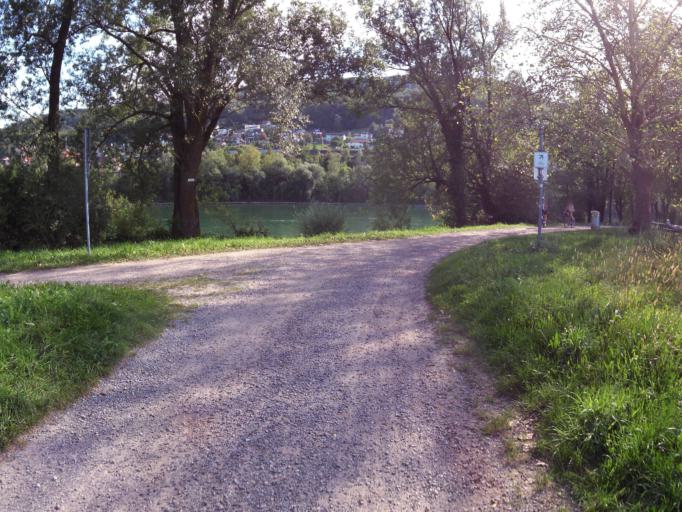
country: CH
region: Aargau
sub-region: Bezirk Rheinfelden
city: Stein
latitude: 47.5452
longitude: 7.9464
